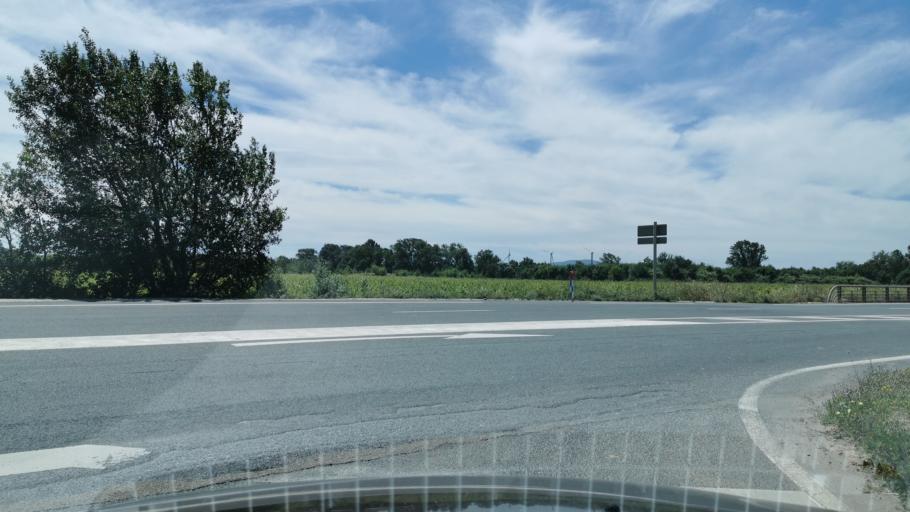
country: FR
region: Languedoc-Roussillon
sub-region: Departement de l'Aude
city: Canet
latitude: 43.2126
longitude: 2.8688
